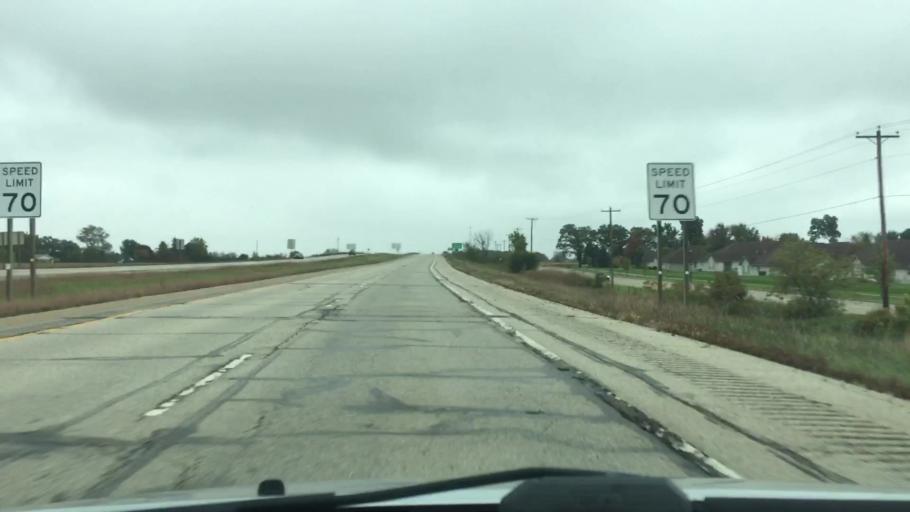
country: US
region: Wisconsin
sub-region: Walworth County
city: Elkhorn
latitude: 42.6872
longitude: -88.5311
